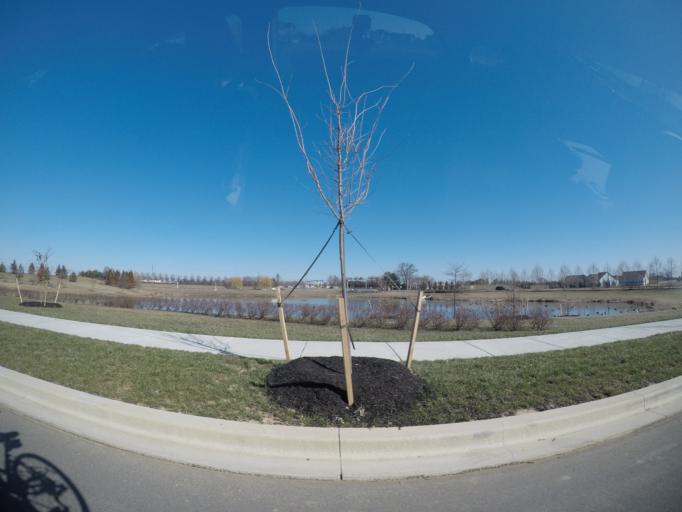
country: US
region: Delaware
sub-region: New Castle County
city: Middletown
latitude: 39.4983
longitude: -75.6690
